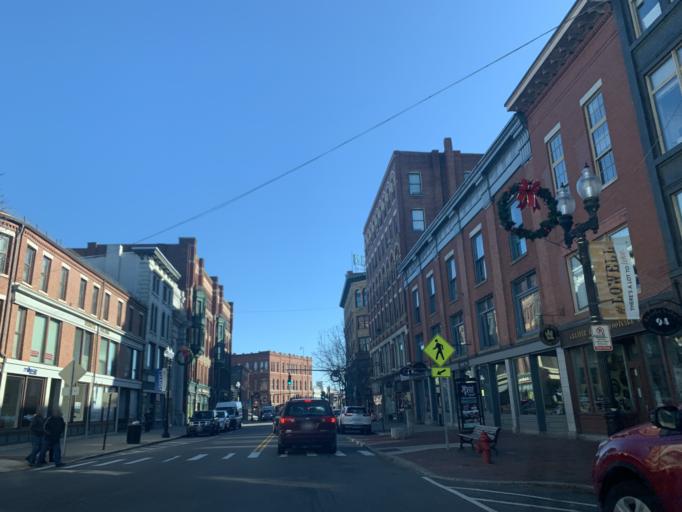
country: US
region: Massachusetts
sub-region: Middlesex County
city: Lowell
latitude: 42.6456
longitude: -71.3094
